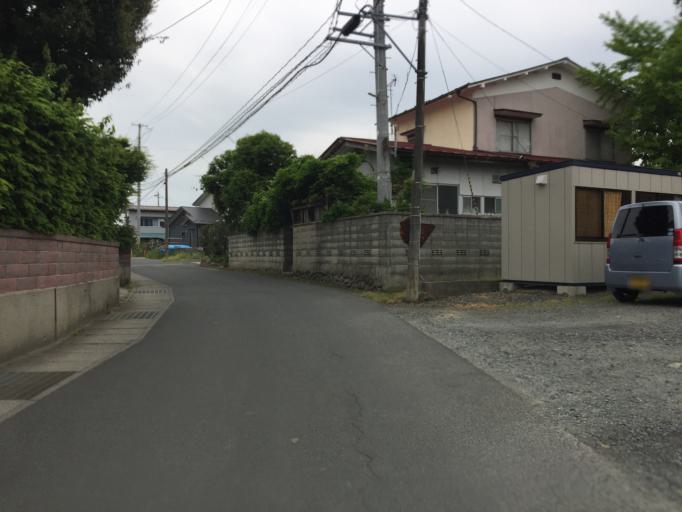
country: JP
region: Fukushima
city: Fukushima-shi
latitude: 37.7954
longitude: 140.4518
